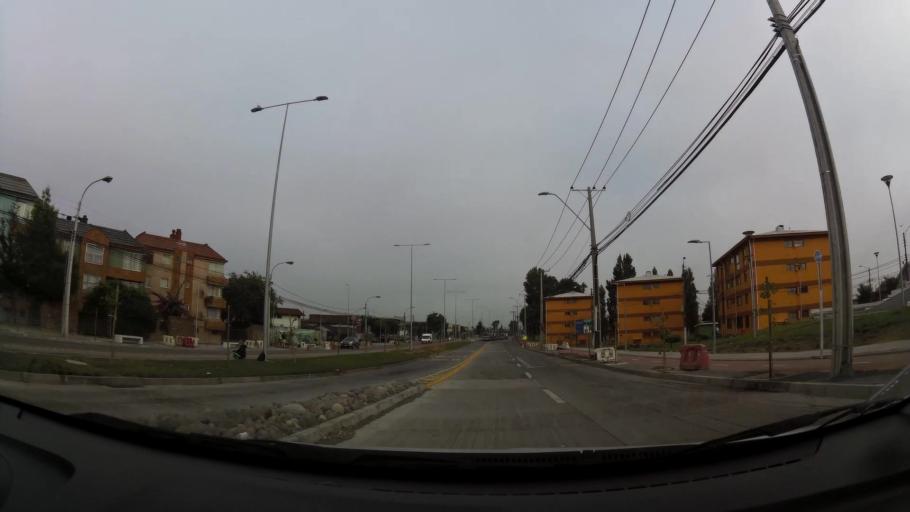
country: CL
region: Biobio
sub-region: Provincia de Concepcion
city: Concepcion
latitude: -36.8023
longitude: -73.0827
